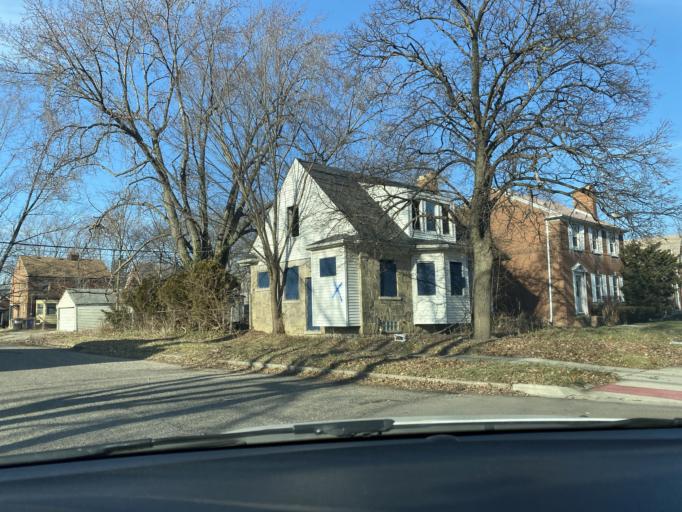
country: US
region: Michigan
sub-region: Wayne County
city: Harper Woods
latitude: 42.4135
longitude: -82.9496
